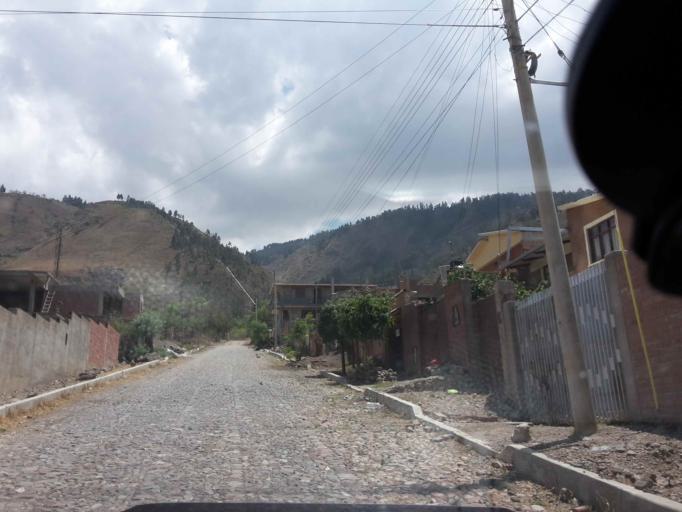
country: BO
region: Cochabamba
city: Cochabamba
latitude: -17.3214
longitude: -66.2226
